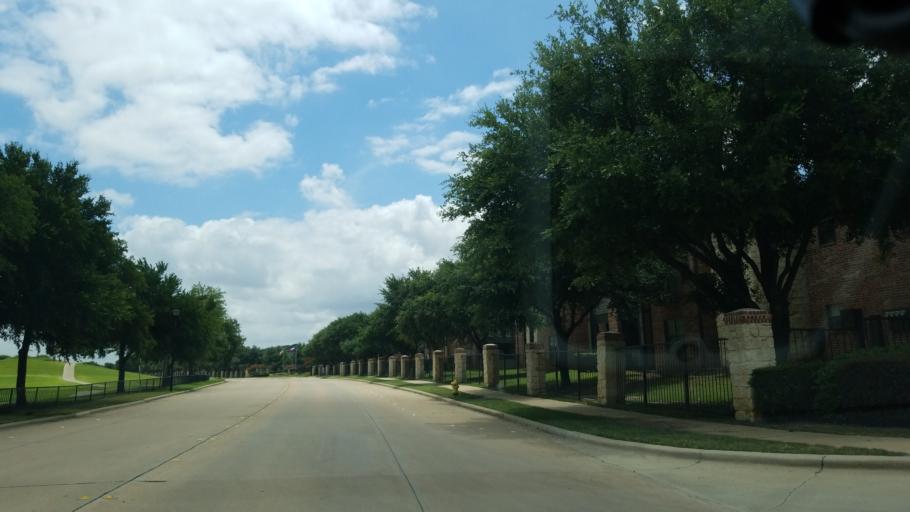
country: US
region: Texas
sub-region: Dallas County
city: Coppell
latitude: 32.9545
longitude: -96.9553
